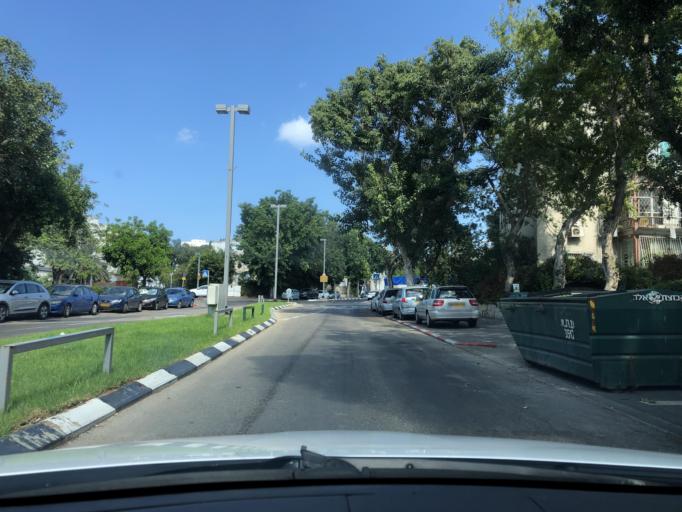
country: IL
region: Tel Aviv
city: Yafo
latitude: 32.0380
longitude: 34.7531
